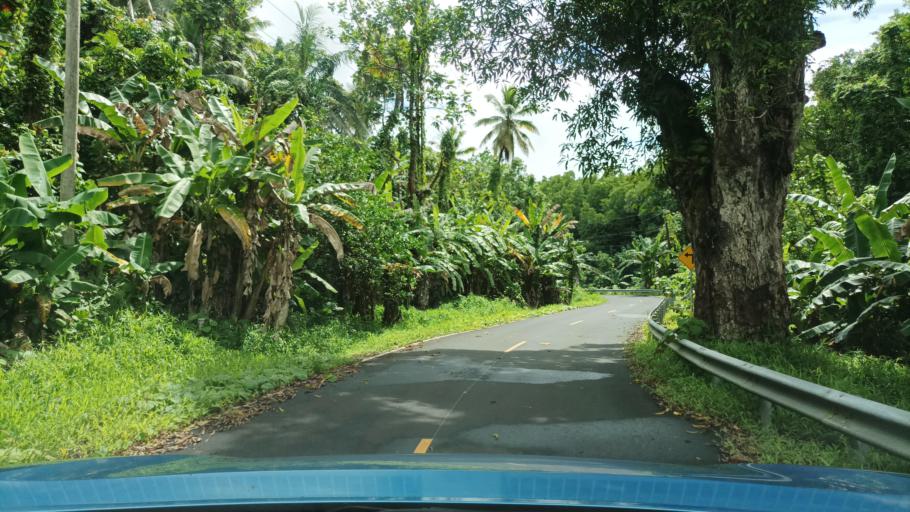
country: FM
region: Pohnpei
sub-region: Madolenihm Municipality
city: Madolenihm Municipality Government
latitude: 6.8712
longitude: 158.3320
